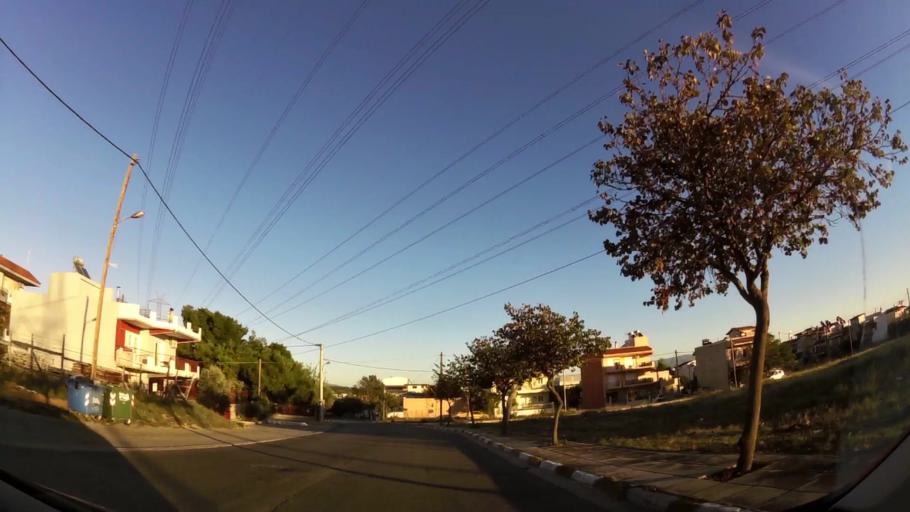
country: GR
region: Attica
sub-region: Nomarchia Dytikis Attikis
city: Ano Liosia
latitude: 38.0916
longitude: 23.7057
